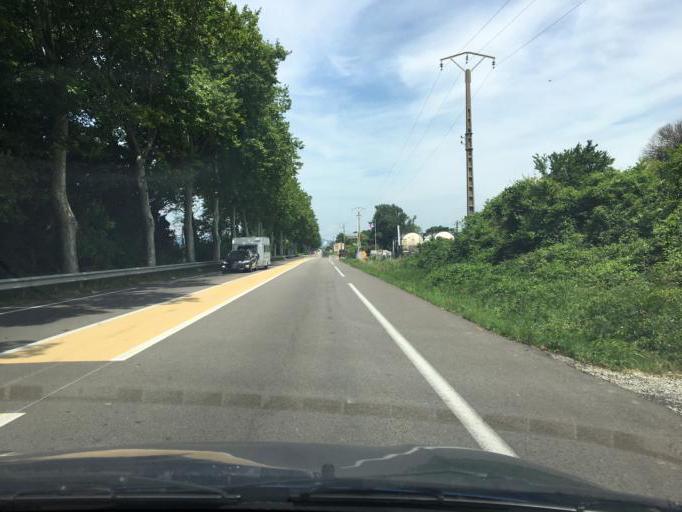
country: FR
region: Rhone-Alpes
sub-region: Departement de la Drome
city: Malataverne
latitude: 44.5061
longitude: 4.7439
